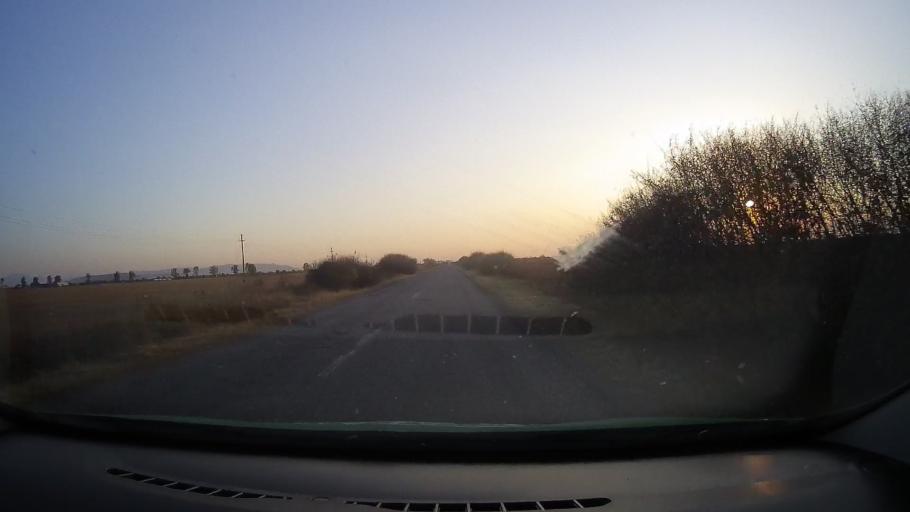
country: RO
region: Arad
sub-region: Comuna Seleus
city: Seleus
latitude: 46.3993
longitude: 21.7220
